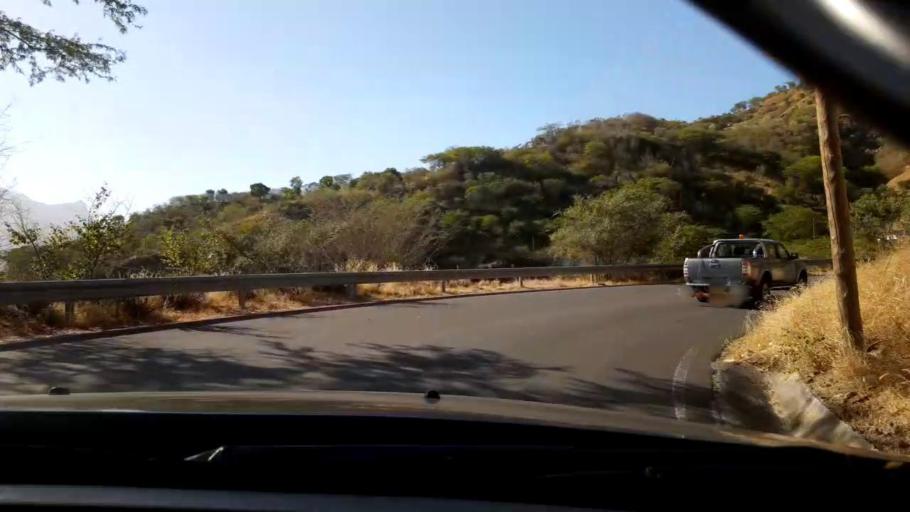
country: CV
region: Sao Lourenco dos Orgaos
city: Joao Teves
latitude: 15.0722
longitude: -23.5663
